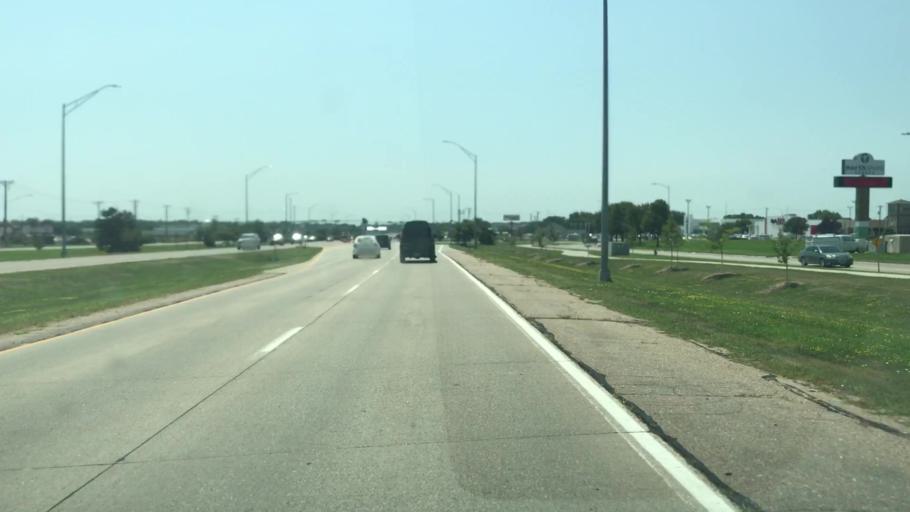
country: US
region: Nebraska
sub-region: Adams County
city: Hastings
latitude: 40.6211
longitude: -98.3830
